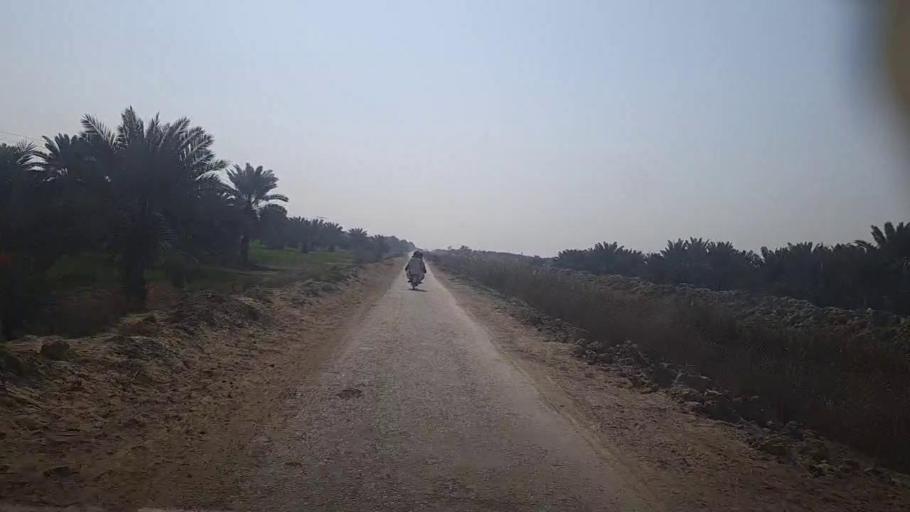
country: PK
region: Sindh
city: Khairpur
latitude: 27.4582
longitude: 68.8152
